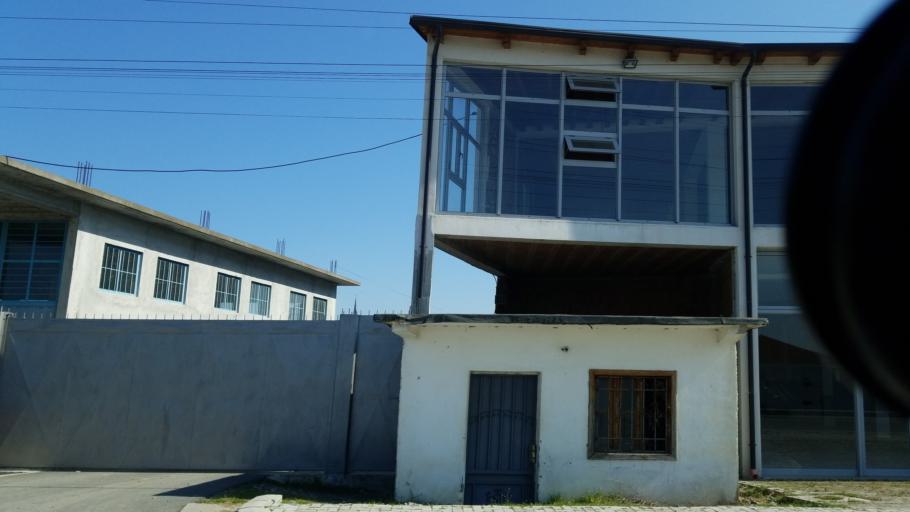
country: AL
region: Shkoder
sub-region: Rrethi i Shkodres
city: Berdica e Madhe
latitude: 41.9805
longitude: 19.4797
